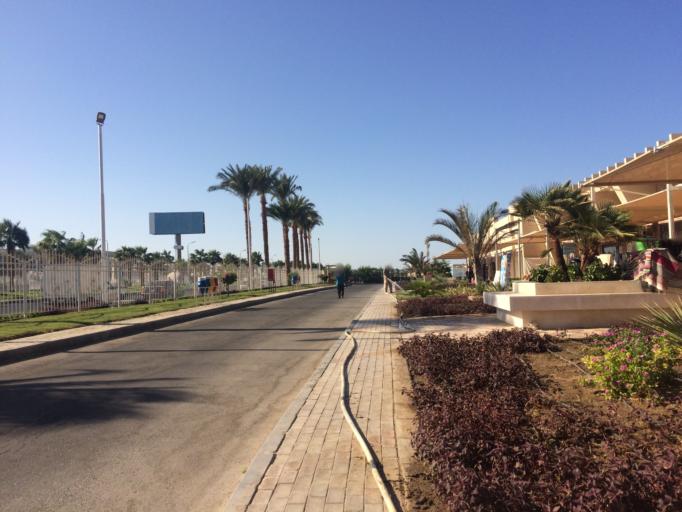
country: EG
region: Red Sea
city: Hurghada
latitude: 27.1223
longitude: 33.8243
